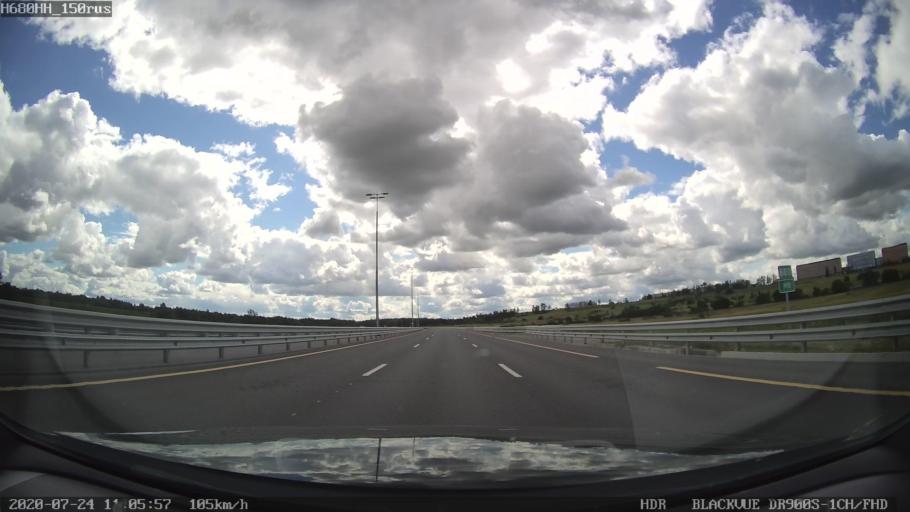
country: RU
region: St.-Petersburg
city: Shushary
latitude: 59.7701
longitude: 30.3646
